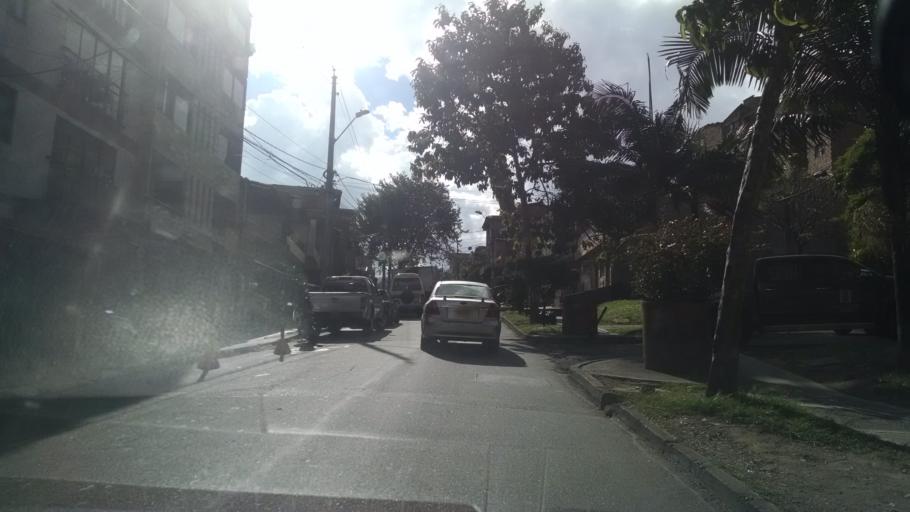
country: CO
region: Antioquia
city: Medellin
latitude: 6.2842
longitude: -75.5848
